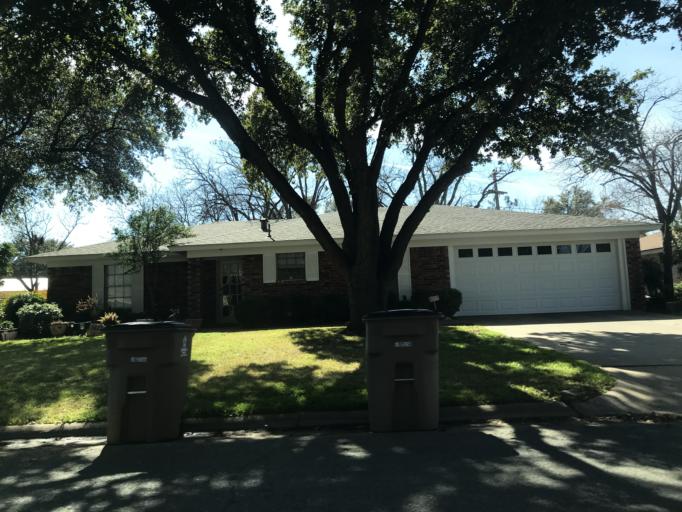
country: US
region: Texas
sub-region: Tom Green County
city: San Angelo
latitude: 31.4344
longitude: -100.4861
